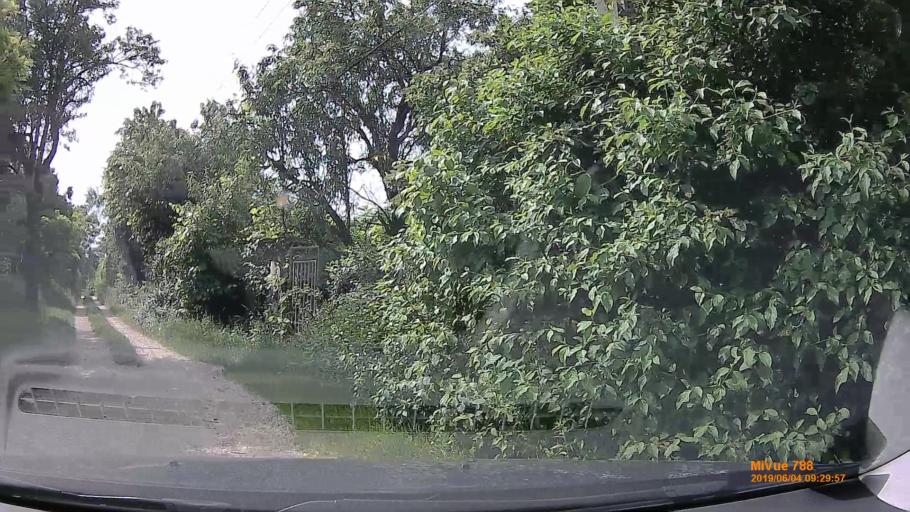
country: HU
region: Pest
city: Diosd
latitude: 47.4129
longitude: 18.9836
